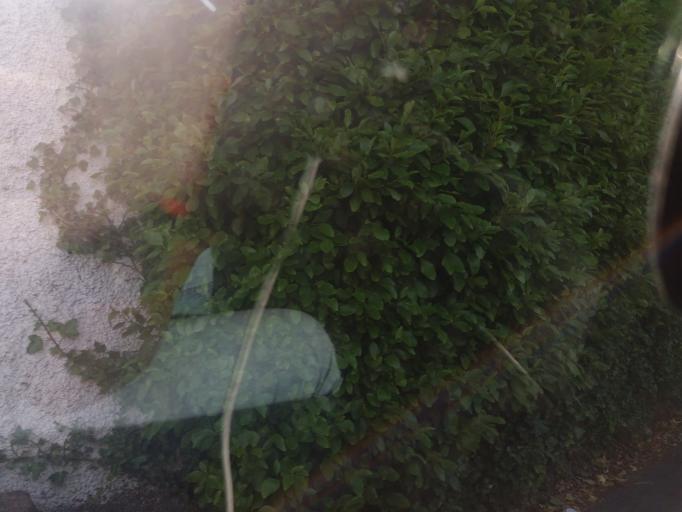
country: IE
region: Leinster
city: Lusk
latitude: 53.5254
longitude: -6.1674
